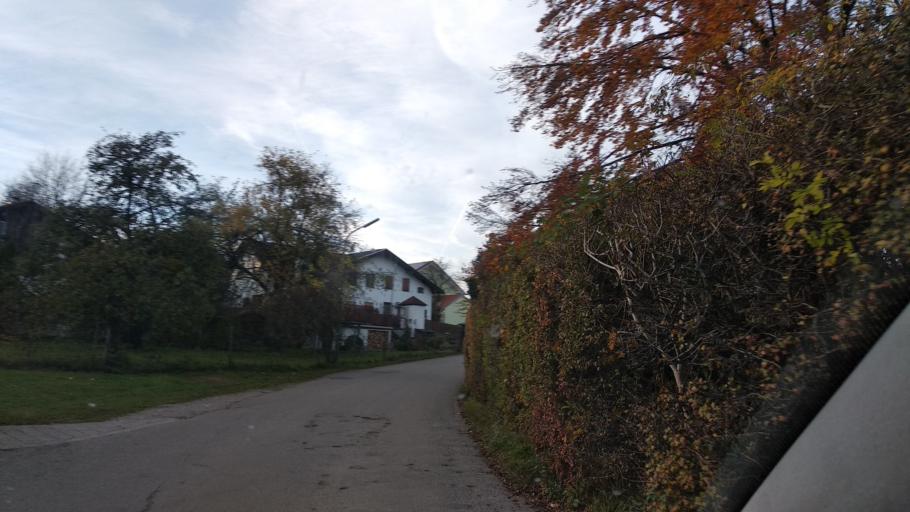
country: DE
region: Bavaria
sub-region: Upper Bavaria
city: Grafing bei Munchen
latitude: 48.0434
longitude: 11.9717
